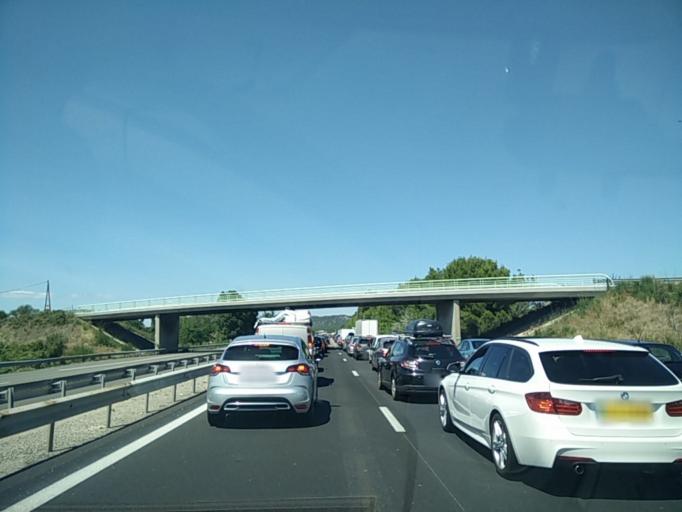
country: FR
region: Provence-Alpes-Cote d'Azur
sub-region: Departement du Vaucluse
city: Piolenc
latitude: 44.1720
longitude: 4.7599
